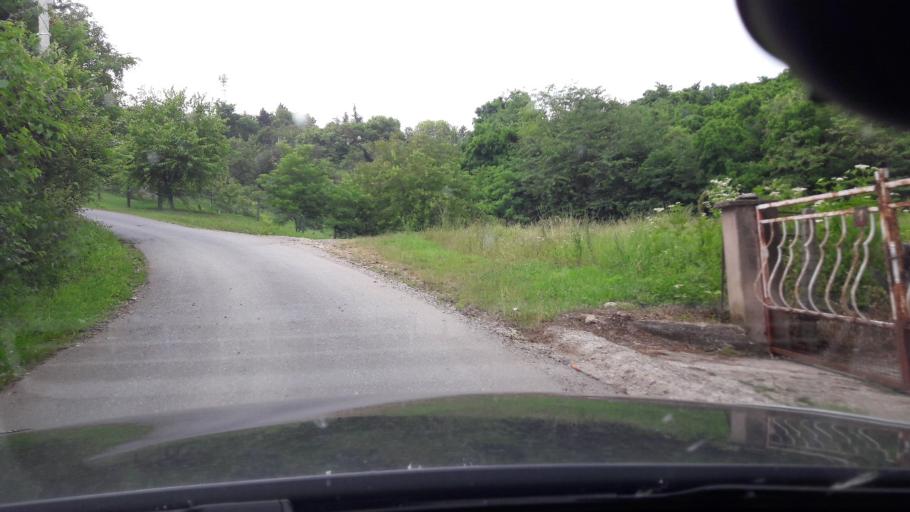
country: RS
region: Central Serbia
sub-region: Belgrade
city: Grocka
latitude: 44.6530
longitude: 20.5966
